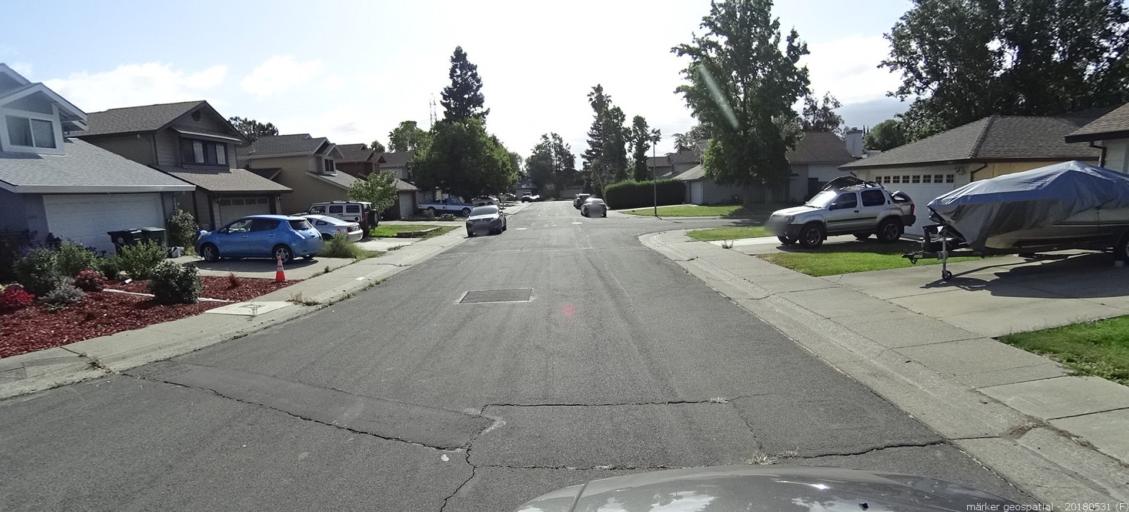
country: US
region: California
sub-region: Sacramento County
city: Sacramento
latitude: 38.6343
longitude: -121.4864
